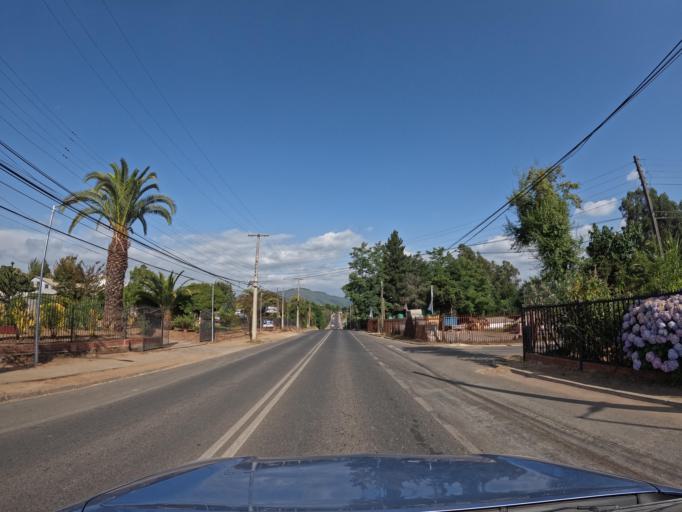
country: CL
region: Maule
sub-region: Provincia de Curico
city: Molina
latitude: -35.2807
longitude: -71.2643
